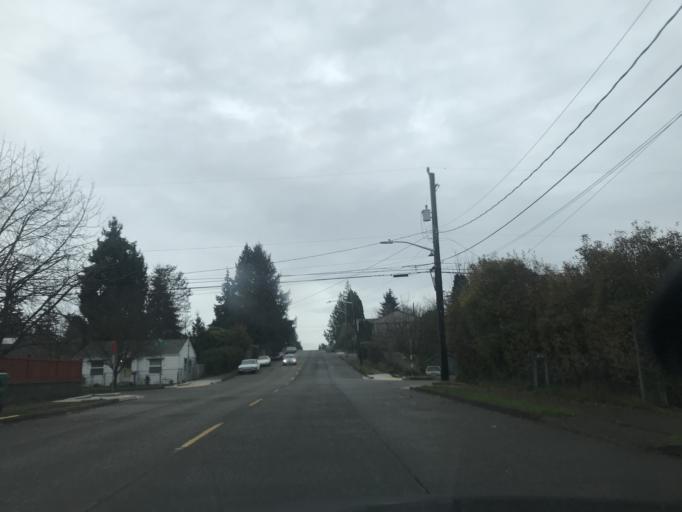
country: US
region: Washington
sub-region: King County
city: White Center
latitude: 47.5229
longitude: -122.3546
